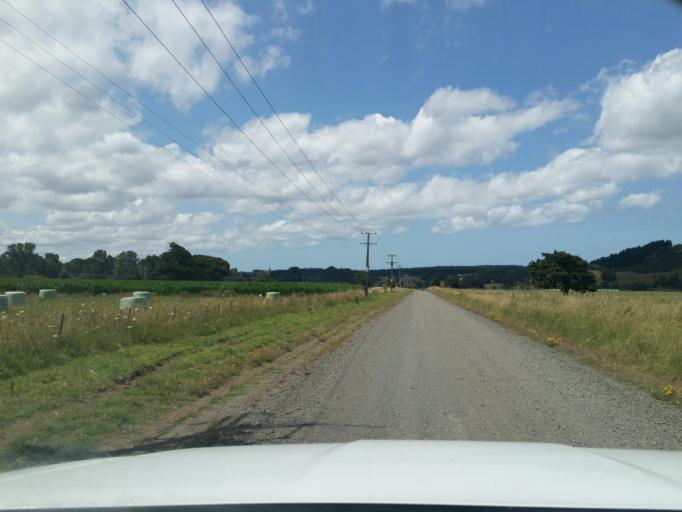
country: NZ
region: Northland
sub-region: Kaipara District
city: Dargaville
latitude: -35.7946
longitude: 173.7319
